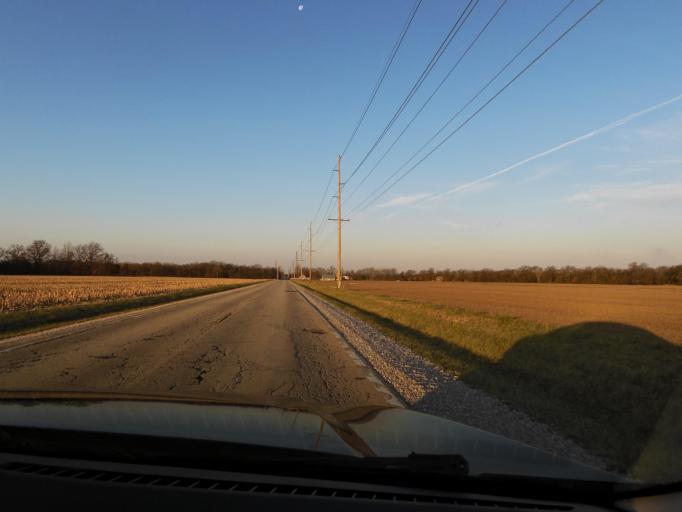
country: US
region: Illinois
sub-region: Marion County
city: Odin
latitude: 38.7650
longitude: -89.0689
